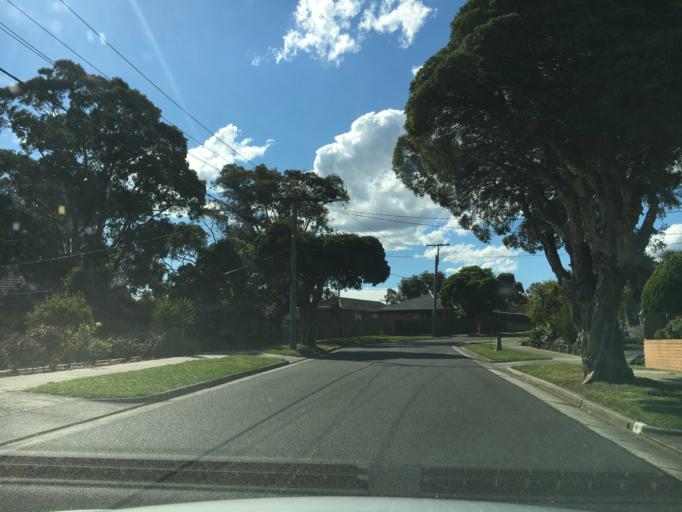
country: AU
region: Victoria
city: Clayton
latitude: -37.9005
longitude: 145.1207
